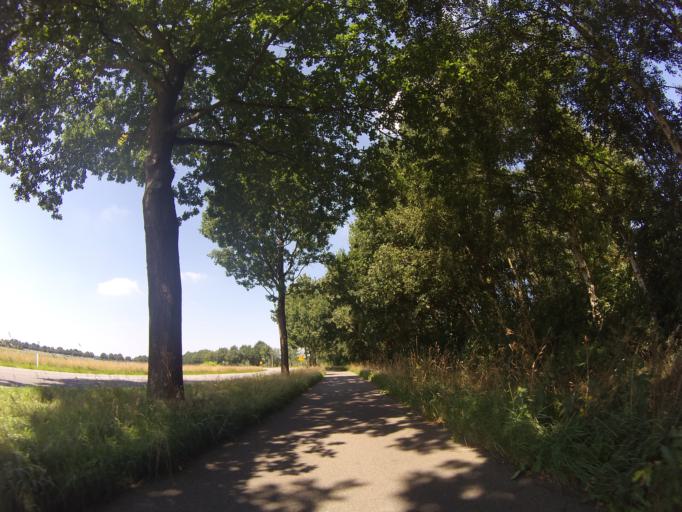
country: NL
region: Drenthe
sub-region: Gemeente Emmen
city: Klazienaveen
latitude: 52.7556
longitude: 7.0203
